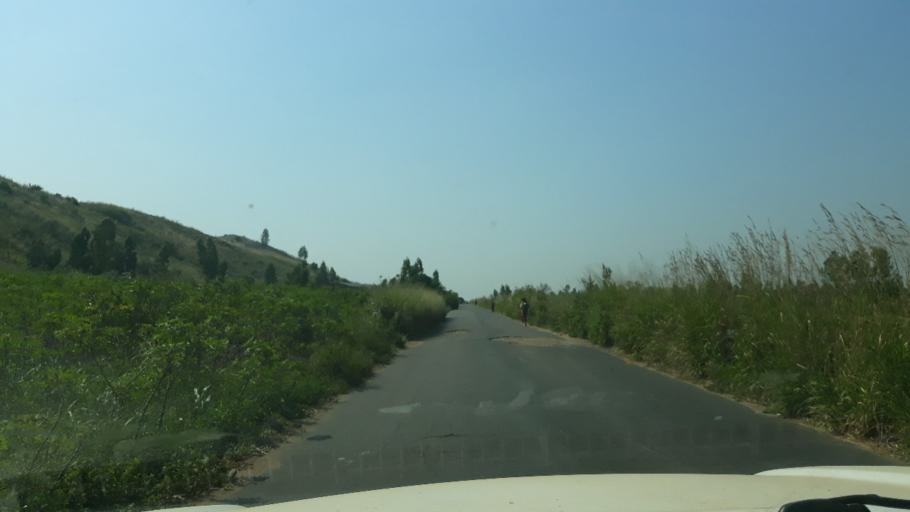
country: CD
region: South Kivu
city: Uvira
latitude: -3.2713
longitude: 29.1612
